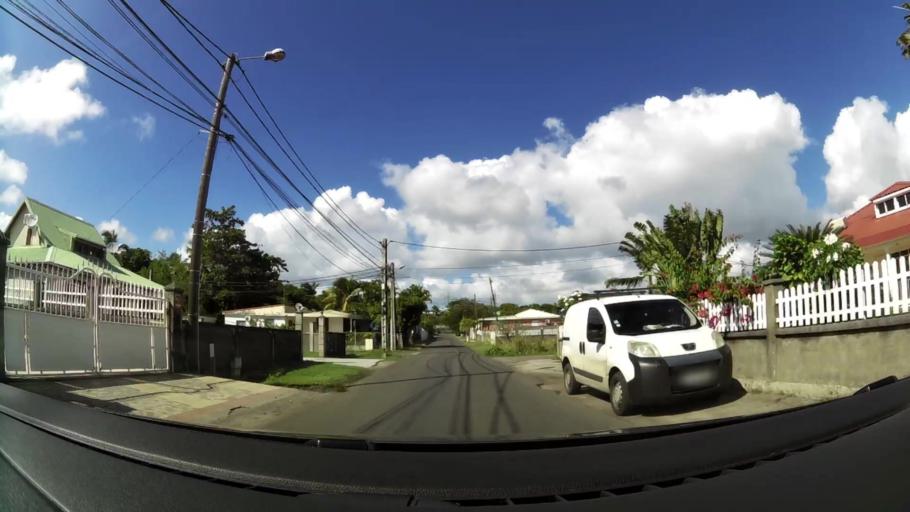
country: GP
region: Guadeloupe
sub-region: Guadeloupe
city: Sainte-Anne
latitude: 16.2296
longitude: -61.3763
